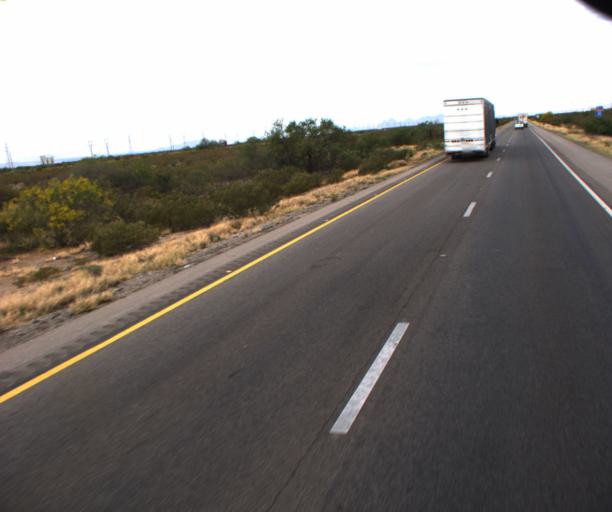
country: US
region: Arizona
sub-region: Pima County
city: Vail
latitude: 32.0337
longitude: -110.7278
